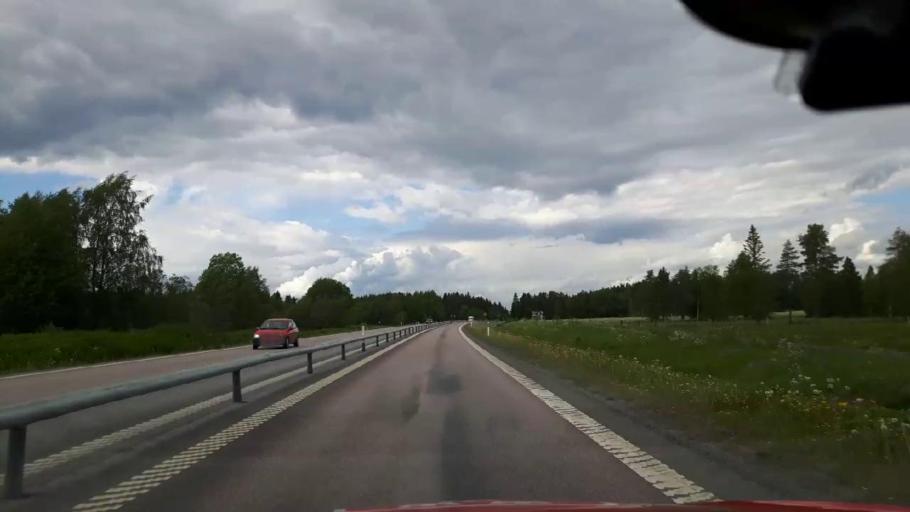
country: SE
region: Jaemtland
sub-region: OEstersunds Kommun
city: Ostersund
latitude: 63.2601
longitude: 14.5511
